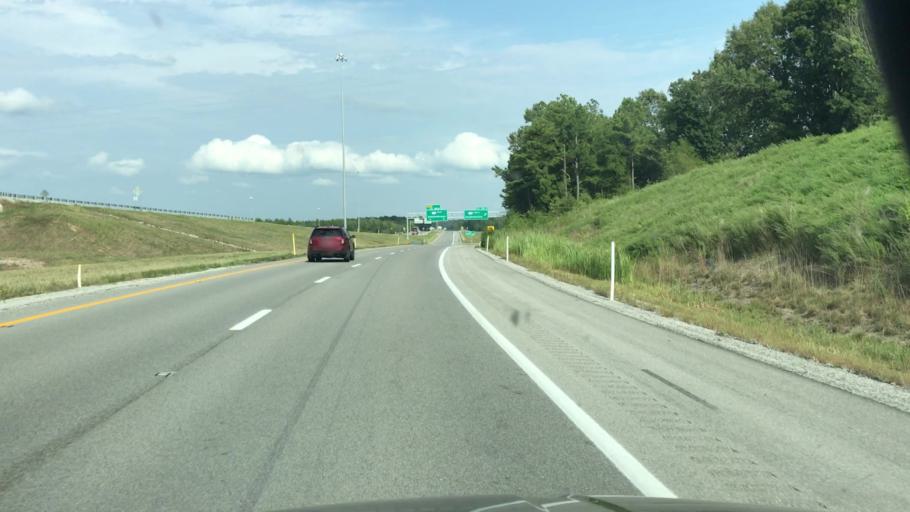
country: US
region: Kentucky
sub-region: Hopkins County
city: Nortonville
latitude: 37.2124
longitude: -87.4491
